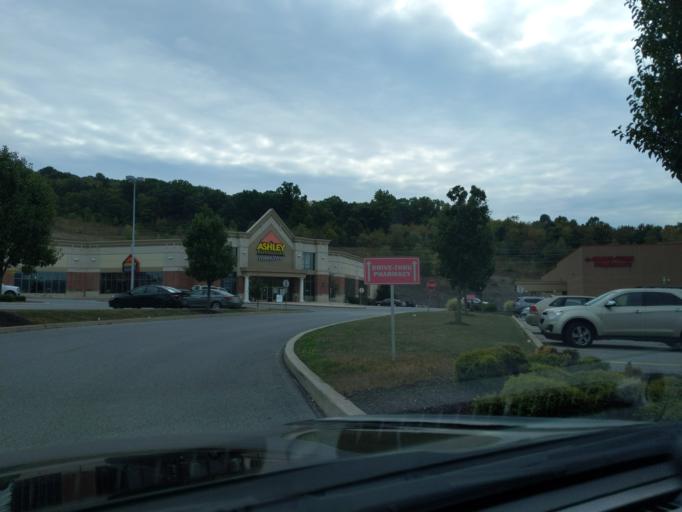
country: US
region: Pennsylvania
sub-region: Blair County
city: Lakemont
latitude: 40.4850
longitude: -78.3867
